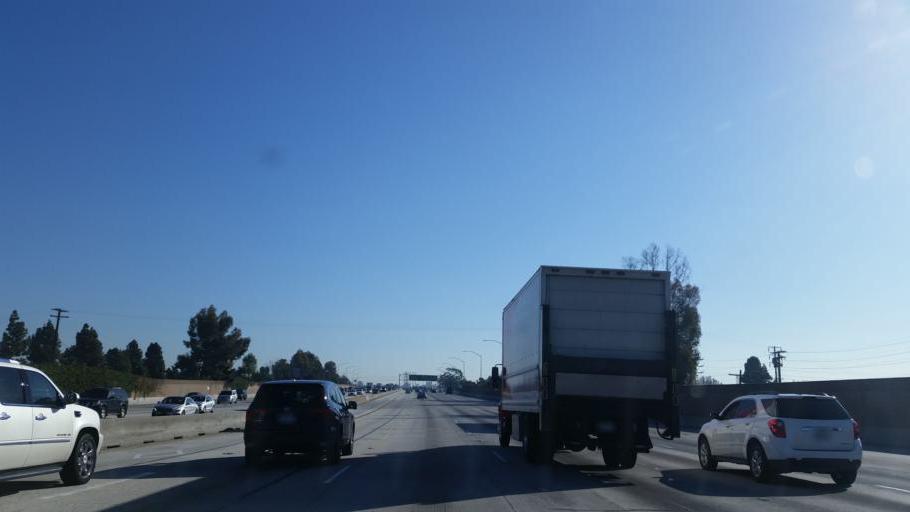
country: US
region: California
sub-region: Los Angeles County
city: Carson
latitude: 33.8252
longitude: -118.2236
